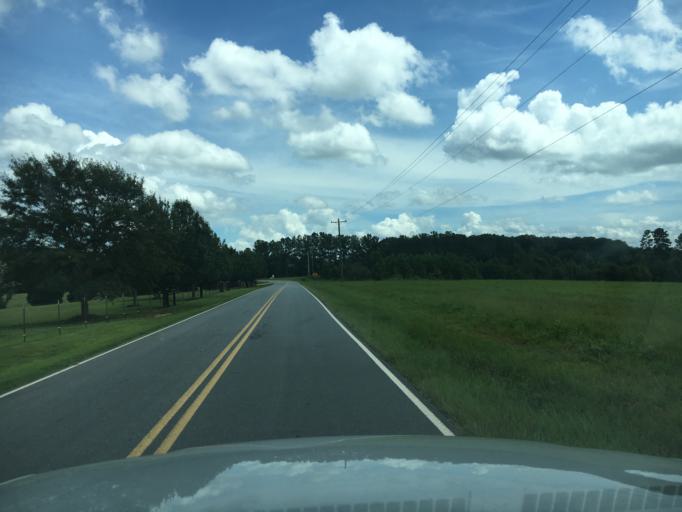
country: US
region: South Carolina
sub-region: Anderson County
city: Belton
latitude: 34.5416
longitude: -82.4490
